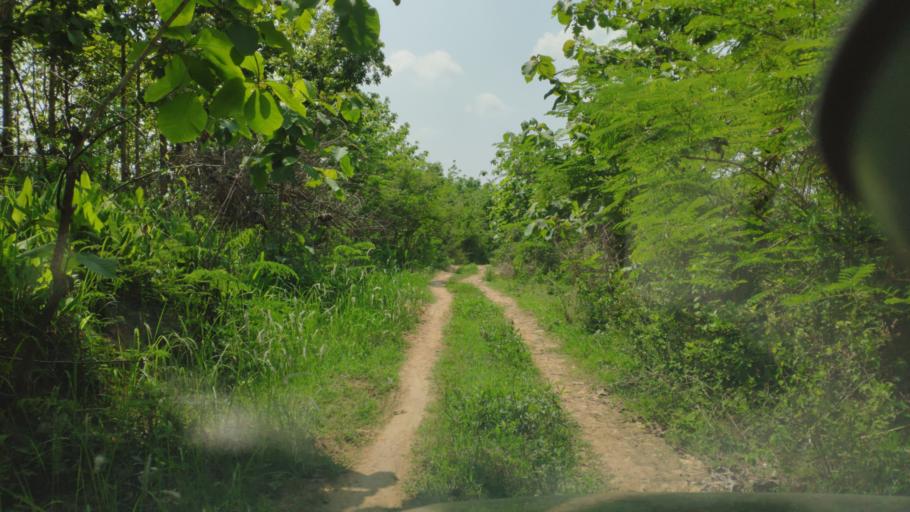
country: ID
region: Central Java
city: Gaplokan
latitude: -6.9141
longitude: 111.2653
